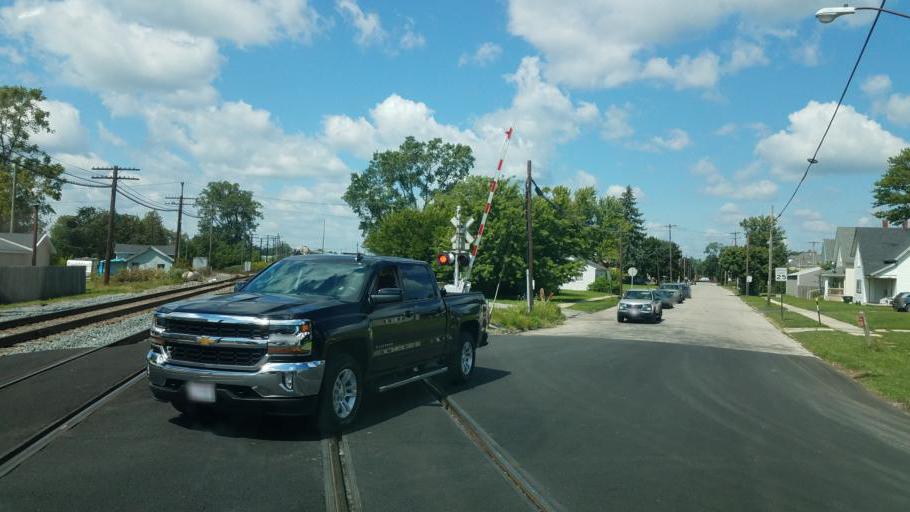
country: US
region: Ohio
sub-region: Seneca County
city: Fostoria
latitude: 41.1513
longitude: -83.4029
